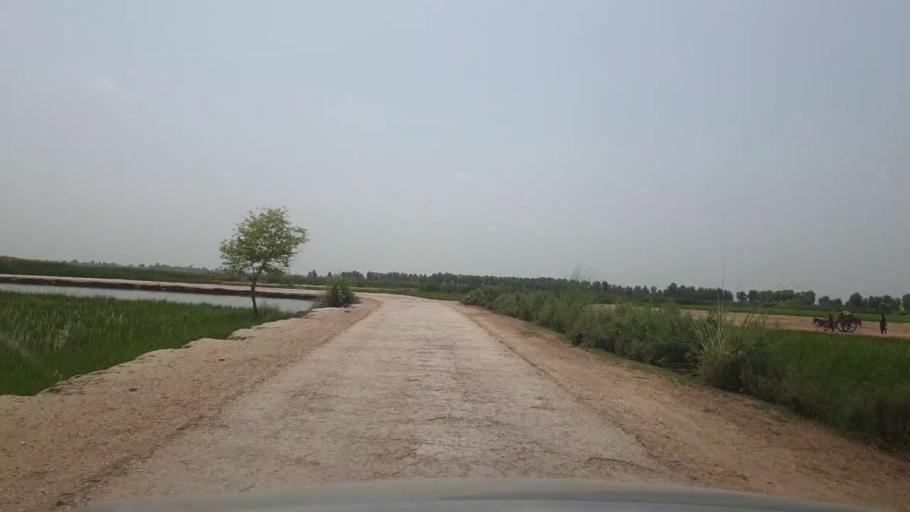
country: PK
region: Sindh
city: Garhi Yasin
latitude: 27.9408
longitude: 68.3804
